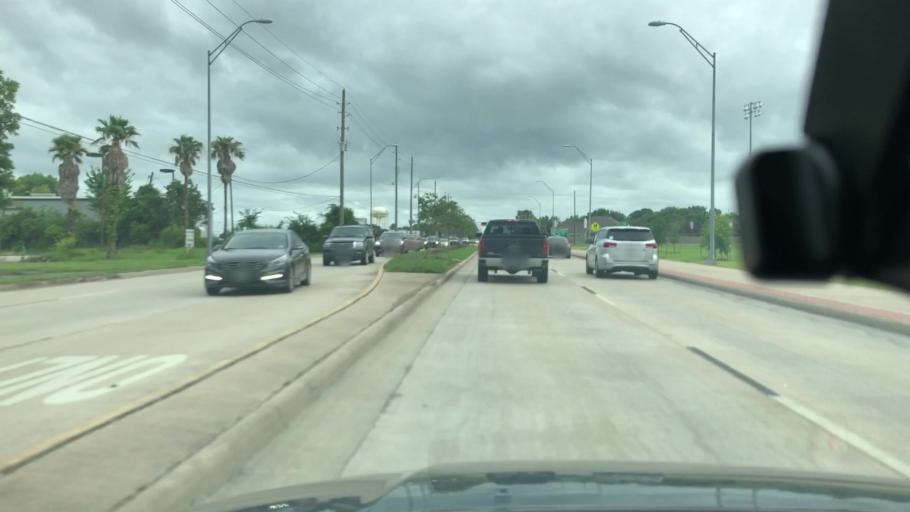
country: US
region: Texas
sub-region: Brazoria County
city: Brookside Village
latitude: 29.5728
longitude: -95.3508
